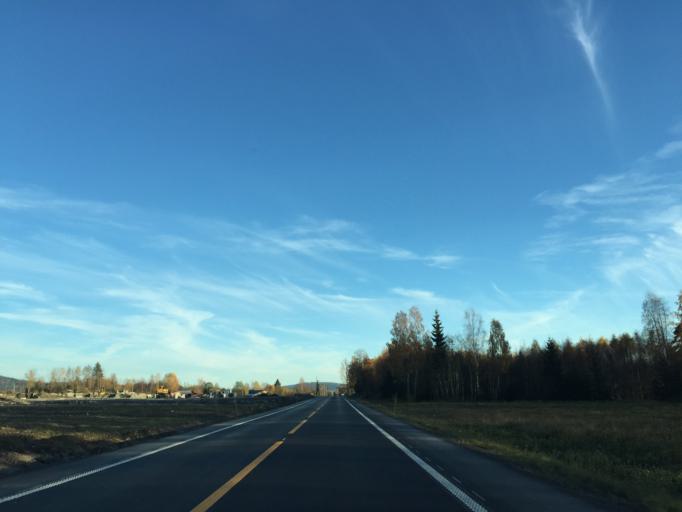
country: NO
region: Hedmark
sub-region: Sor-Odal
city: Skarnes
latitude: 60.2408
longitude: 11.7870
